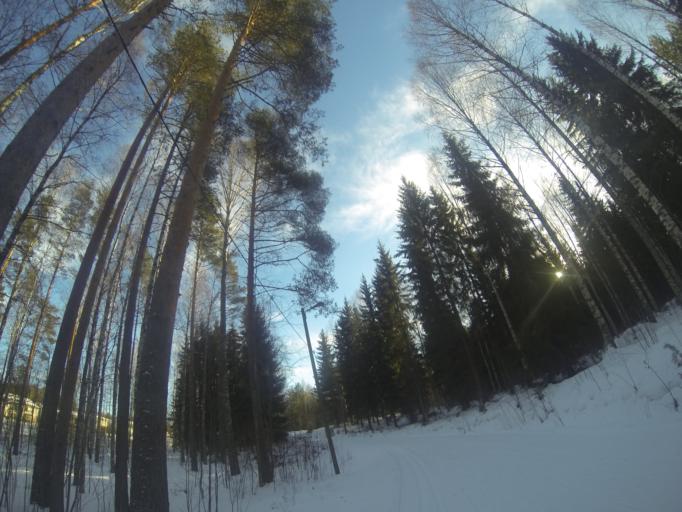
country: FI
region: Southern Savonia
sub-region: Savonlinna
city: Savonlinna
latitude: 61.8794
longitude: 28.9268
